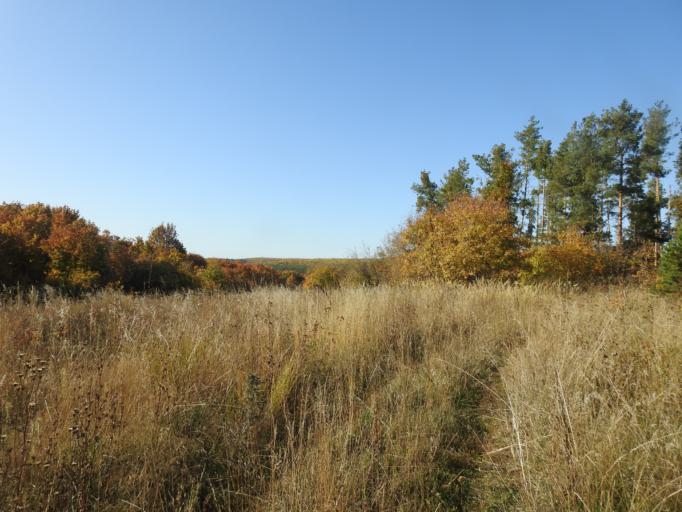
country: RU
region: Saratov
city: Baltay
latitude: 52.4989
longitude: 46.7477
